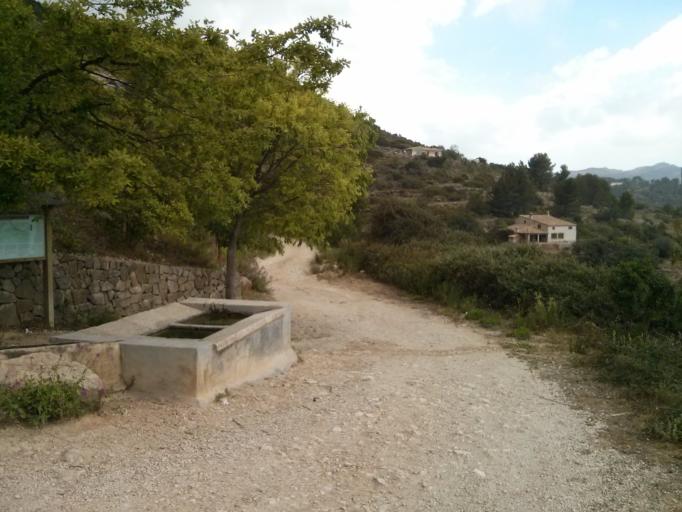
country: ES
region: Valencia
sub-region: Provincia de Alicante
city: Altea
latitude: 38.6647
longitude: -0.0394
